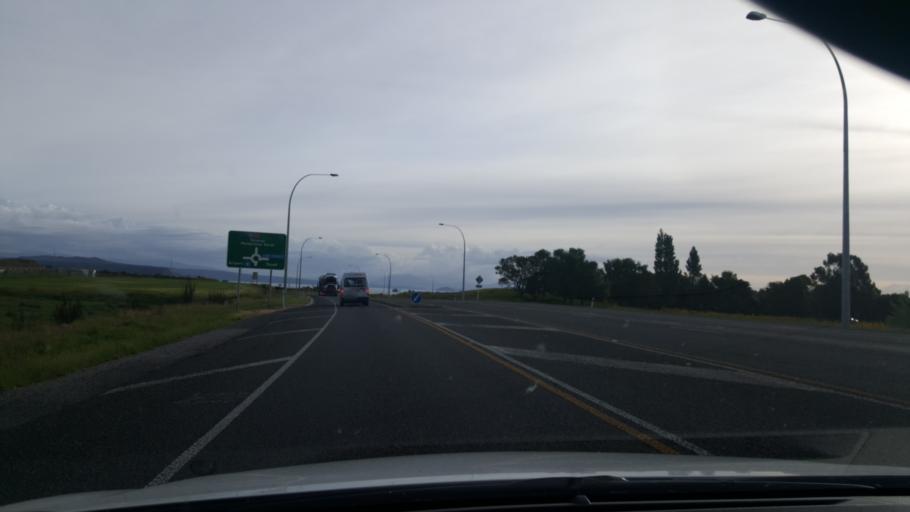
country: NZ
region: Waikato
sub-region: Taupo District
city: Taupo
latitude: -38.7366
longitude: 176.0745
